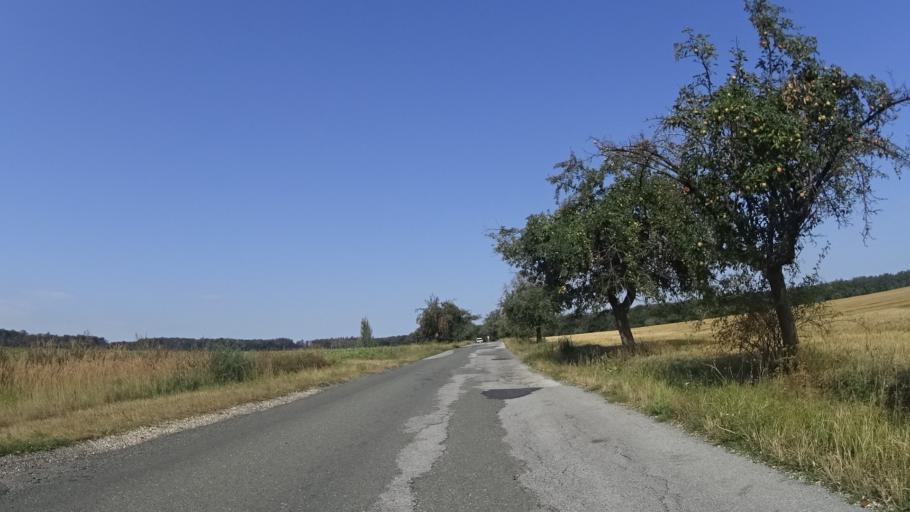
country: CZ
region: Kralovehradecky
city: Novy Bydzov
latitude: 50.2786
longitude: 15.5460
